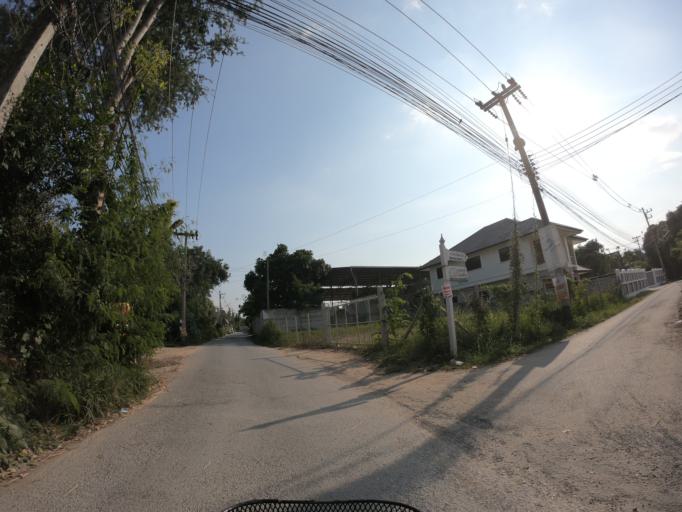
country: TH
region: Chiang Mai
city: Chiang Mai
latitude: 18.8354
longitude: 98.9858
